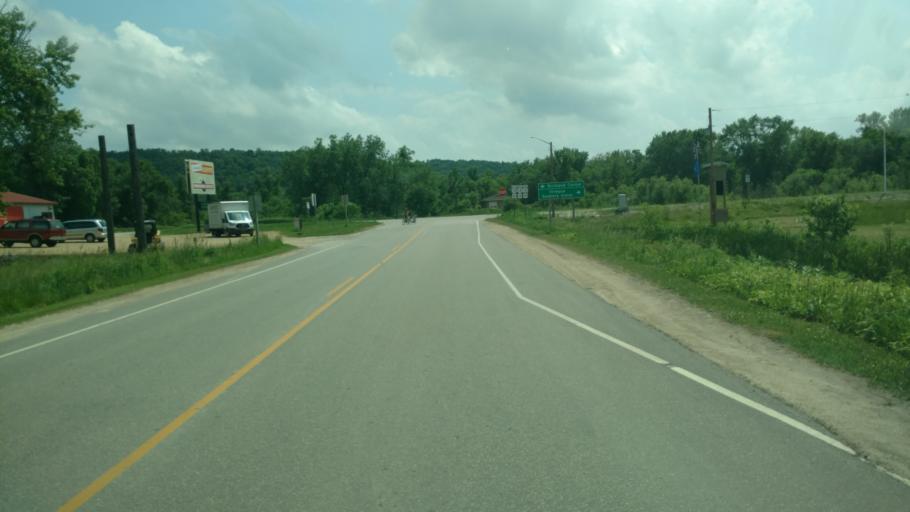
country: US
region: Wisconsin
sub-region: Vernon County
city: Viroqua
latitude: 43.4454
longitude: -90.7603
